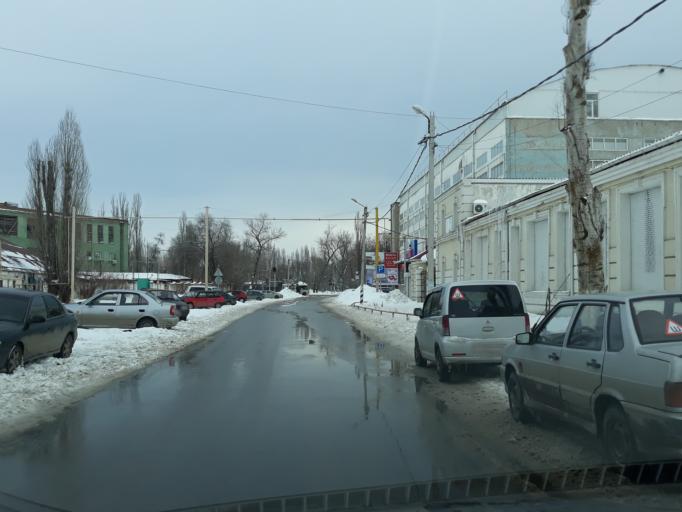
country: RU
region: Rostov
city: Taganrog
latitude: 47.2155
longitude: 38.9355
